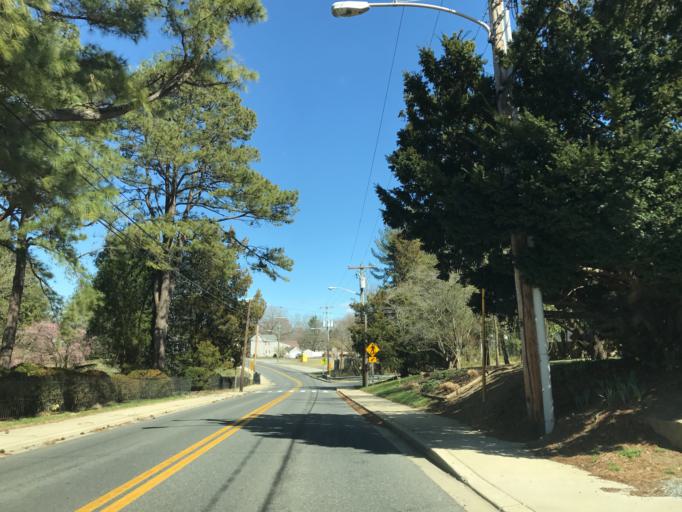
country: US
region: Maryland
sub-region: Queen Anne's County
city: Kingstown
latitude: 39.1447
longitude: -75.9823
